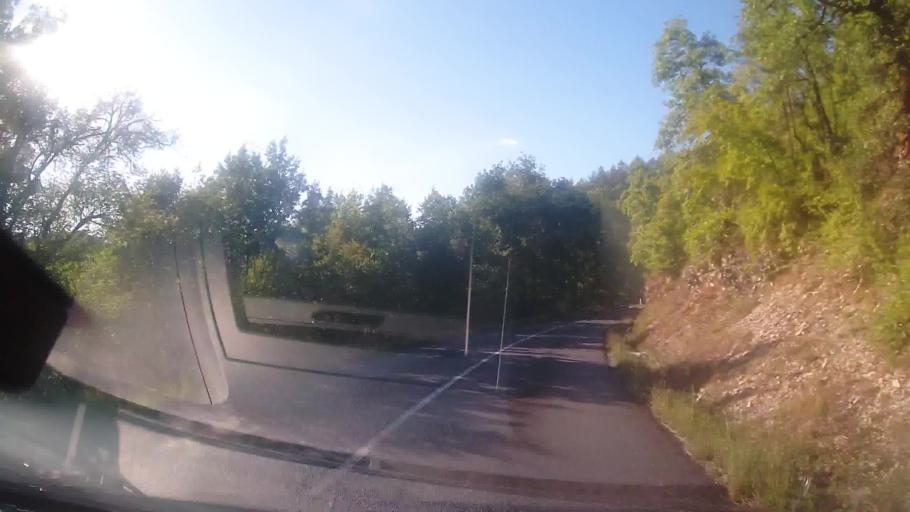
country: FR
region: Aquitaine
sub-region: Departement de la Dordogne
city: Cenac-et-Saint-Julien
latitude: 44.7881
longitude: 1.1786
